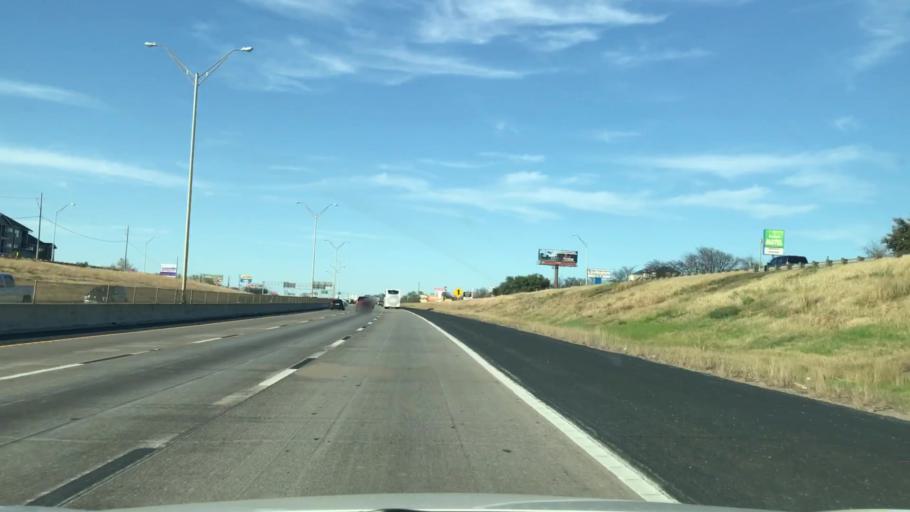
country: US
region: Texas
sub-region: Tarrant County
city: Everman
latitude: 32.6015
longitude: -97.3194
